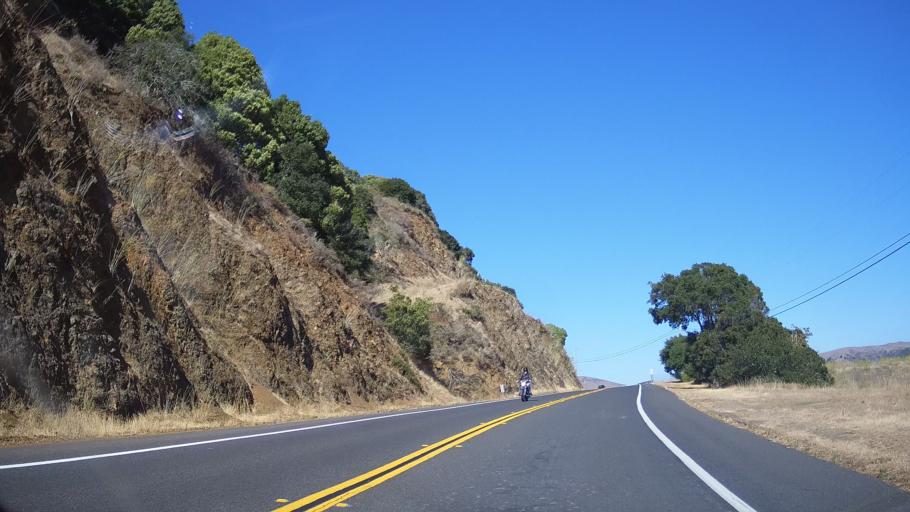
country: US
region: California
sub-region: Marin County
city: Lagunitas-Forest Knolls
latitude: 38.0761
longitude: -122.7564
